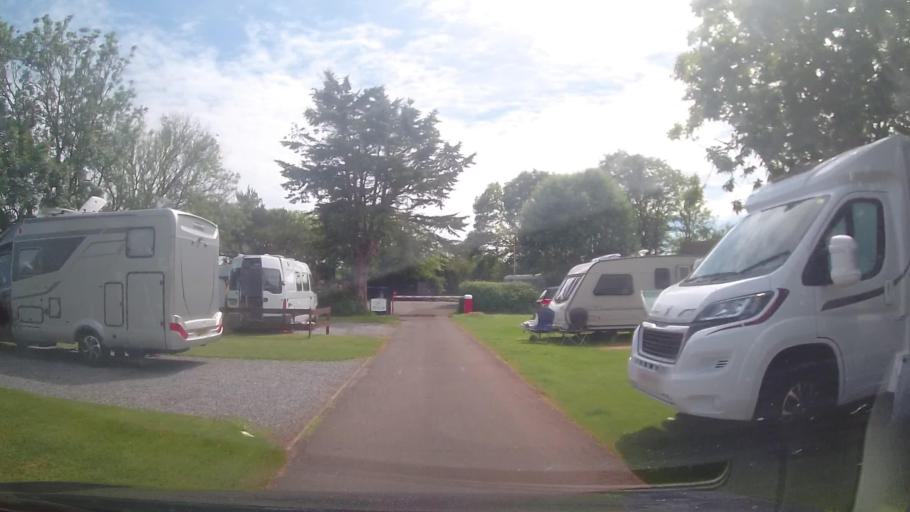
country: GB
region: England
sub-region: Devon
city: Dartmouth
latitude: 50.2911
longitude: -3.6504
